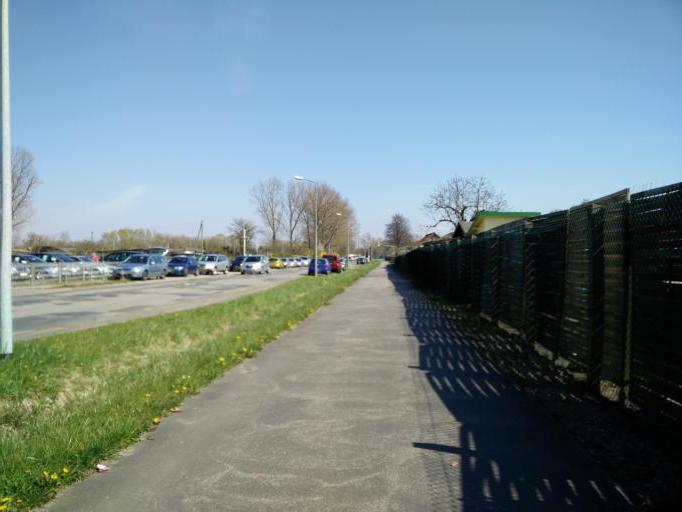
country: DE
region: Mecklenburg-Vorpommern
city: Lambrechtshagen
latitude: 54.1136
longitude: 12.0724
